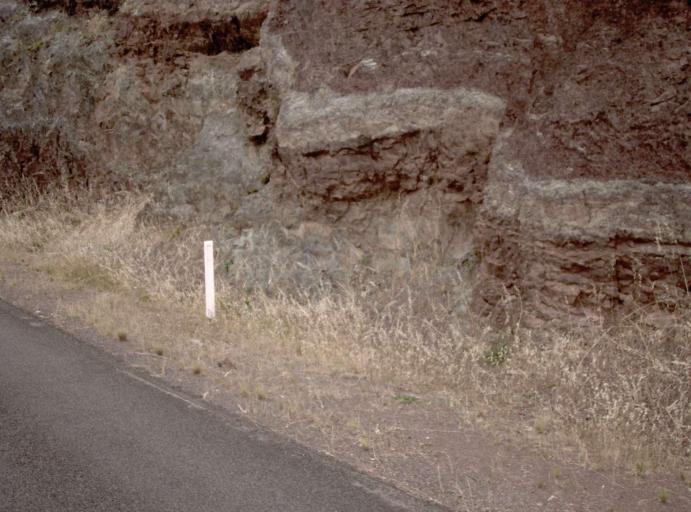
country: AU
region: Victoria
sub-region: Wellington
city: Heyfield
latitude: -37.6654
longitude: 146.6459
